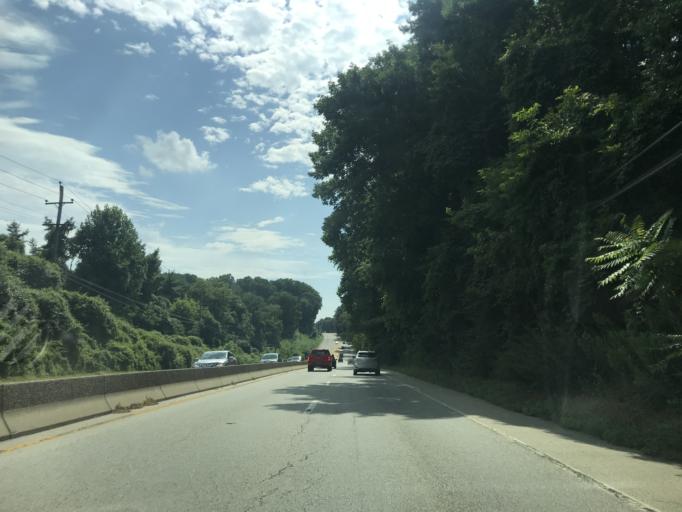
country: US
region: Pennsylvania
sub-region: Chester County
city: Kennett Square
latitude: 39.8740
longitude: -75.6392
